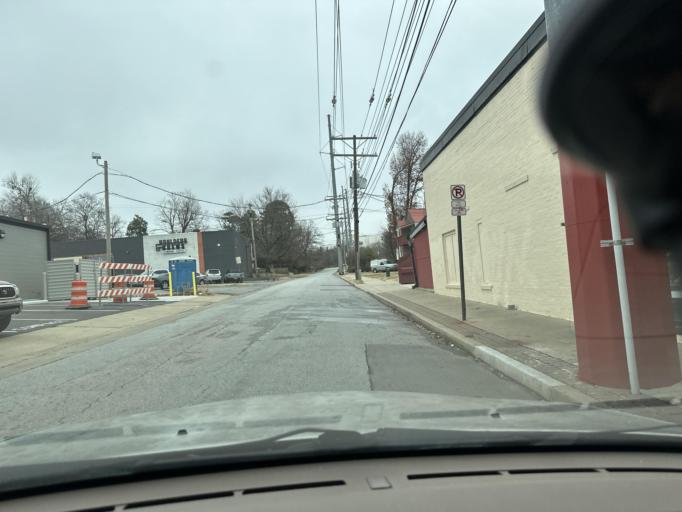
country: US
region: Arkansas
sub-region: Washington County
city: Fayetteville
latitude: 36.0666
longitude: -94.1668
